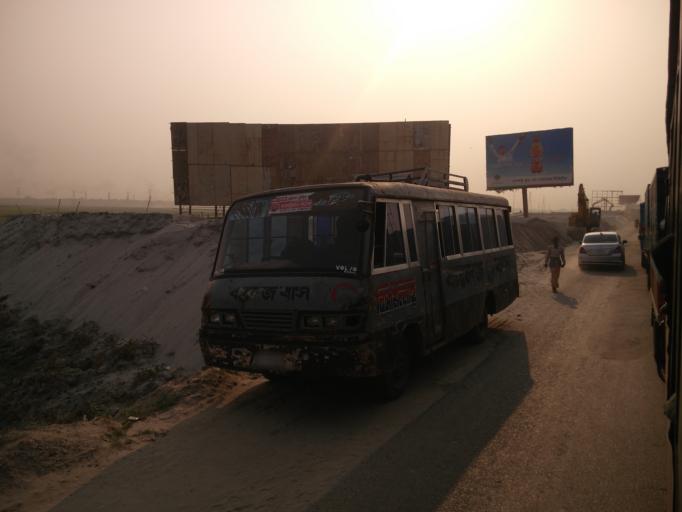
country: BD
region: Dhaka
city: Tungi
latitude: 23.8927
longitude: 90.3590
